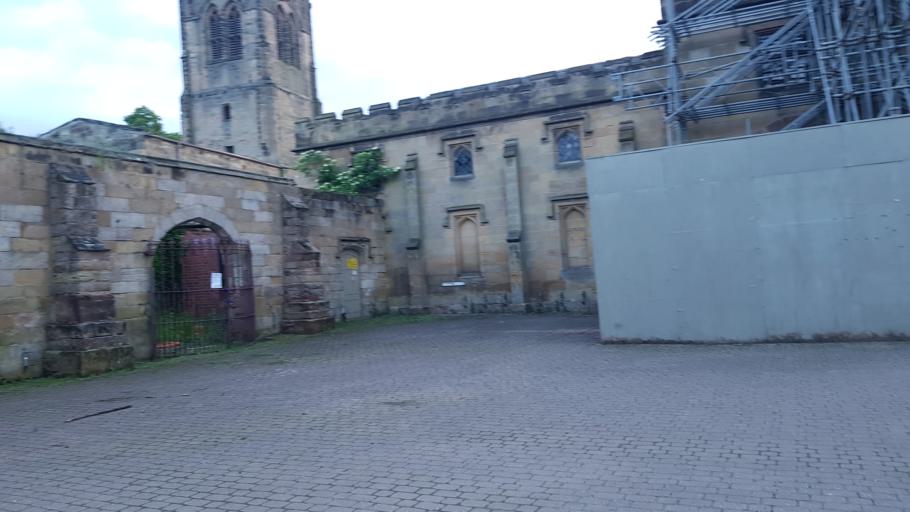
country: GB
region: England
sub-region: Derbyshire
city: Borrowash
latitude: 52.8930
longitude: -1.3959
